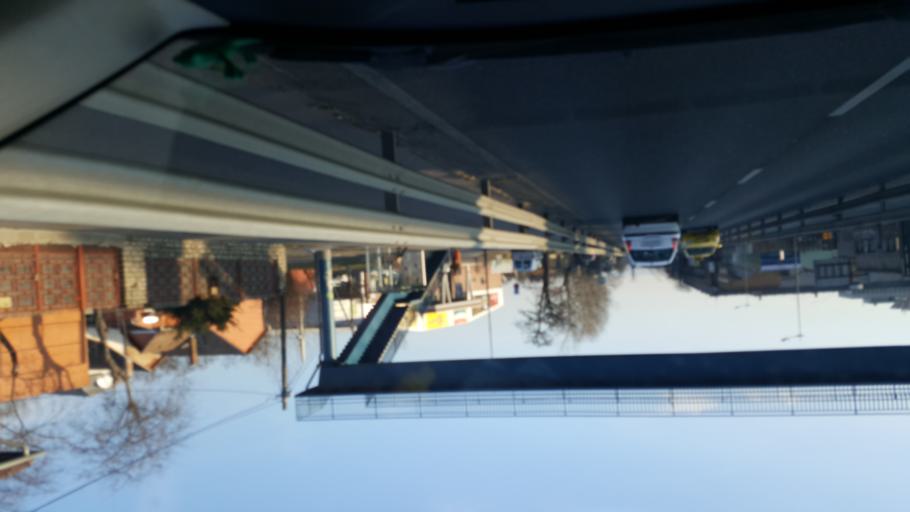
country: HU
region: Budapest
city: Budapest XVIII. keruelet
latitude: 47.4562
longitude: 19.1834
